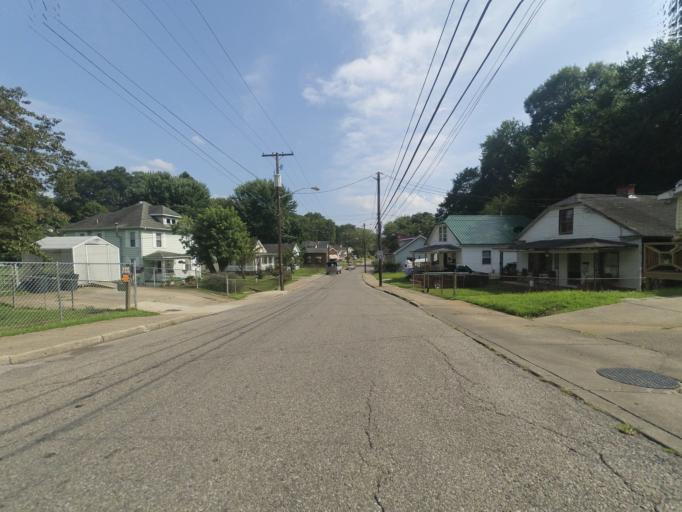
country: US
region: West Virginia
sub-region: Cabell County
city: Huntington
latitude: 38.4145
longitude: -82.4020
